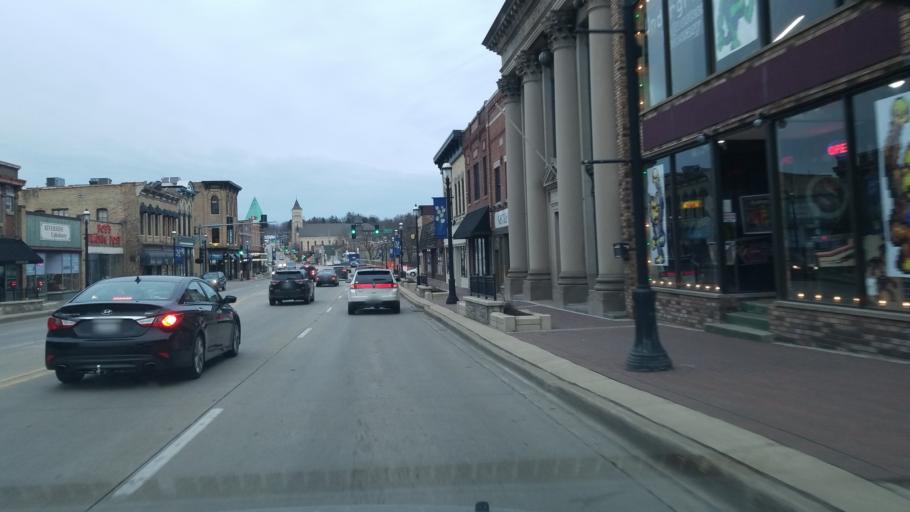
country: US
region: Illinois
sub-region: Kane County
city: West Dundee
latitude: 42.0981
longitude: -88.2783
